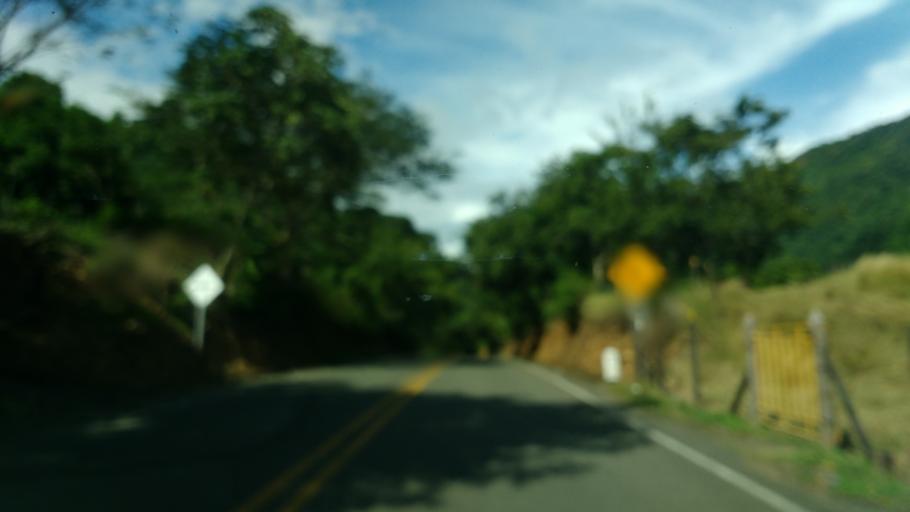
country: CO
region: Antioquia
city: Concordia
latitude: 6.0578
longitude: -75.8666
